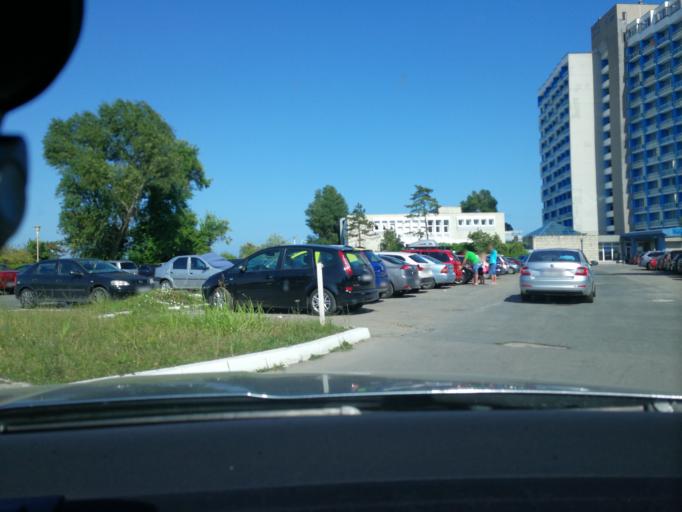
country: RO
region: Constanta
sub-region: Municipiul Mangalia
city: Mangalia
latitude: 43.8315
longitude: 28.5876
